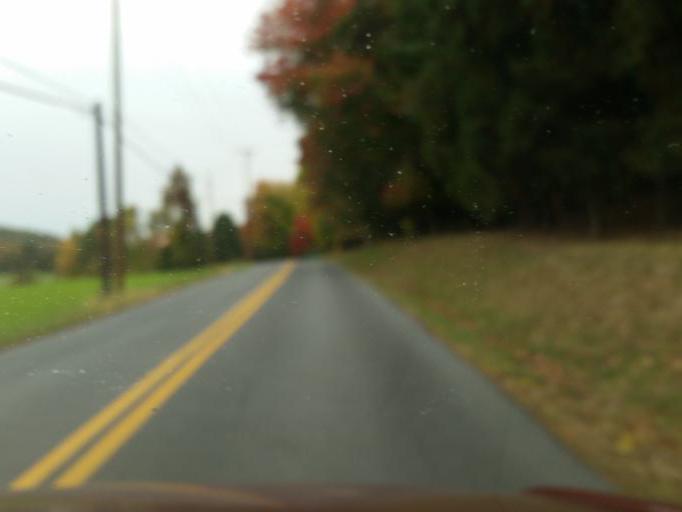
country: US
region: Pennsylvania
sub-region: Dauphin County
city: Hummelstown
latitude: 40.2341
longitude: -76.6828
